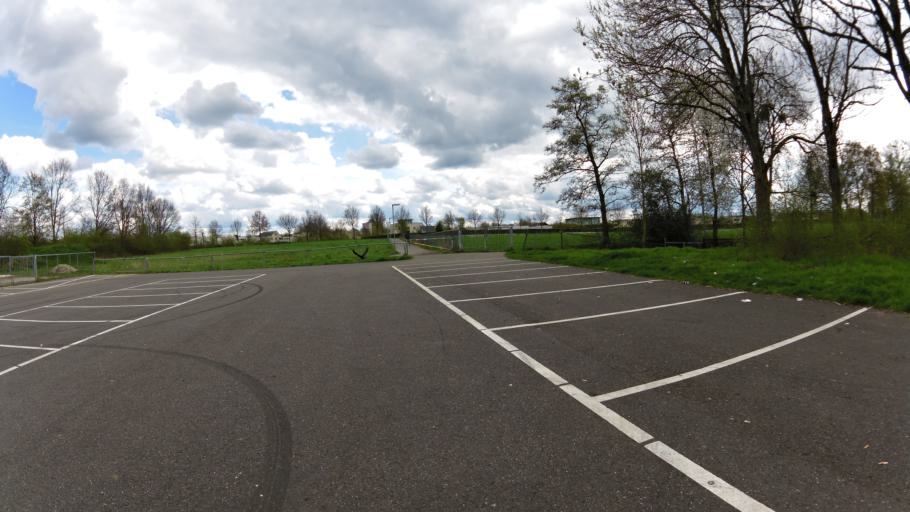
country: NL
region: Limburg
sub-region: Gemeente Heerlen
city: Heerlen
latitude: 50.8777
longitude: 6.0038
